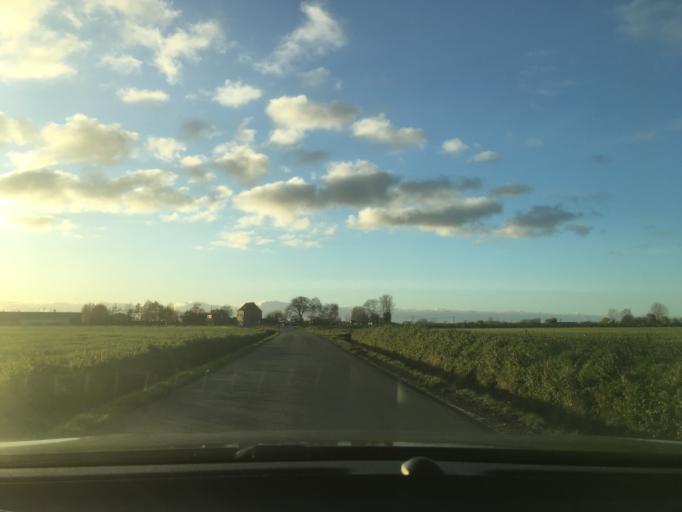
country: BE
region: Flanders
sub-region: Provincie West-Vlaanderen
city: Menen
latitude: 50.8248
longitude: 3.1111
